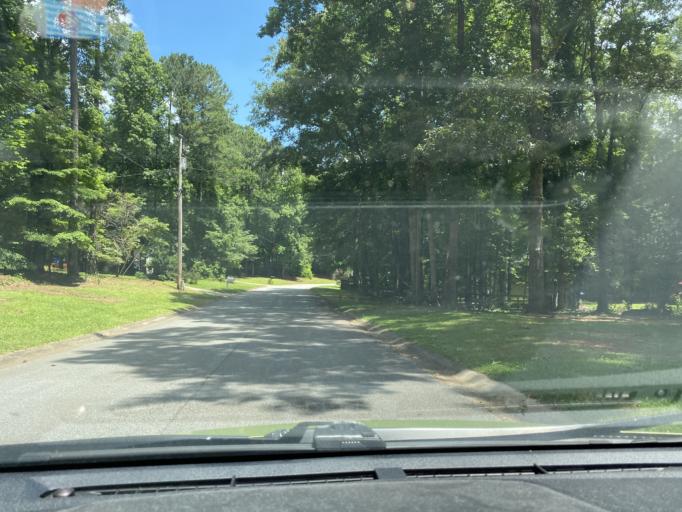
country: US
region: Georgia
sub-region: Fulton County
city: Palmetto
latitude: 33.4356
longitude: -84.6835
